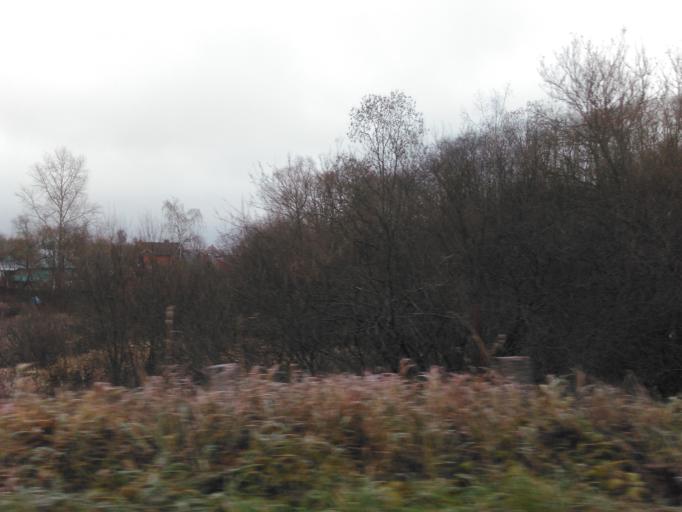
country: RU
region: Moskovskaya
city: Muranovo
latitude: 56.1753
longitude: 37.9040
